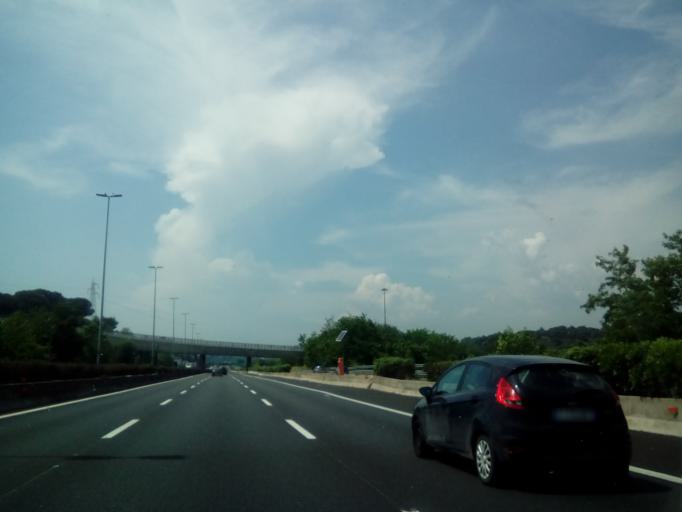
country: IT
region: Latium
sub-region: Citta metropolitana di Roma Capitale
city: Colle Verde
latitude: 41.9829
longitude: 12.5268
